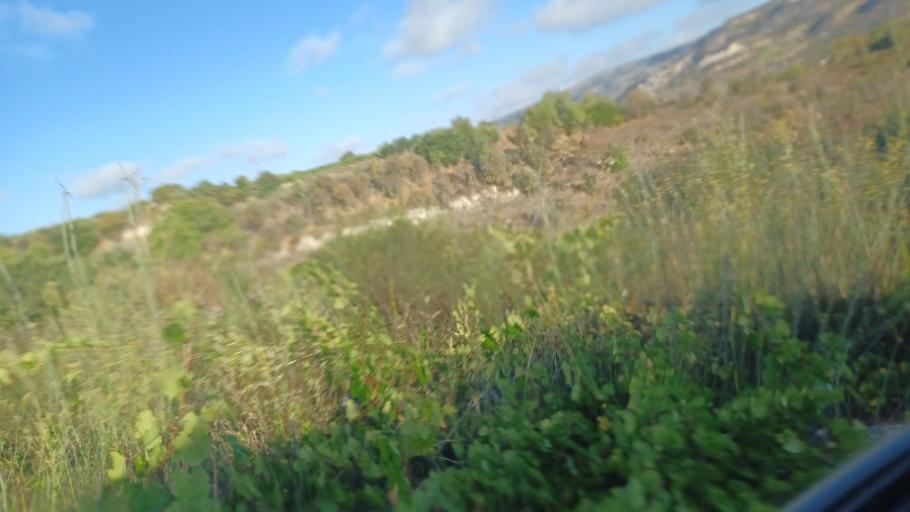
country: CY
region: Pafos
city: Tala
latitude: 34.8677
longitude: 32.4744
